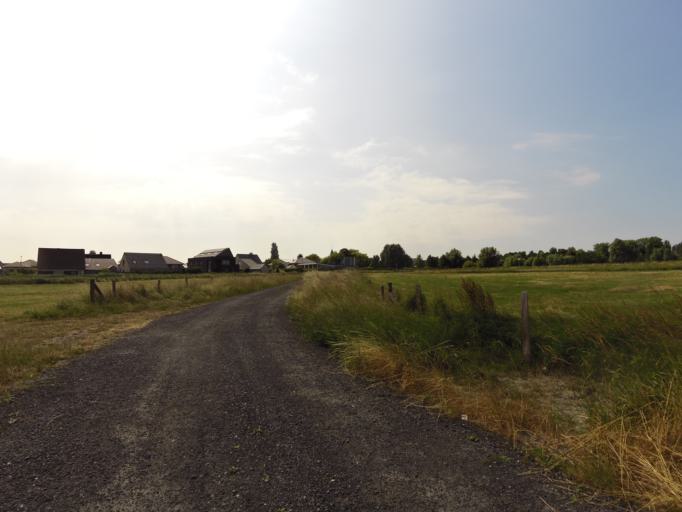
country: BE
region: Flanders
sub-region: Provincie West-Vlaanderen
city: Oudenburg
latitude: 51.2008
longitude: 2.9819
